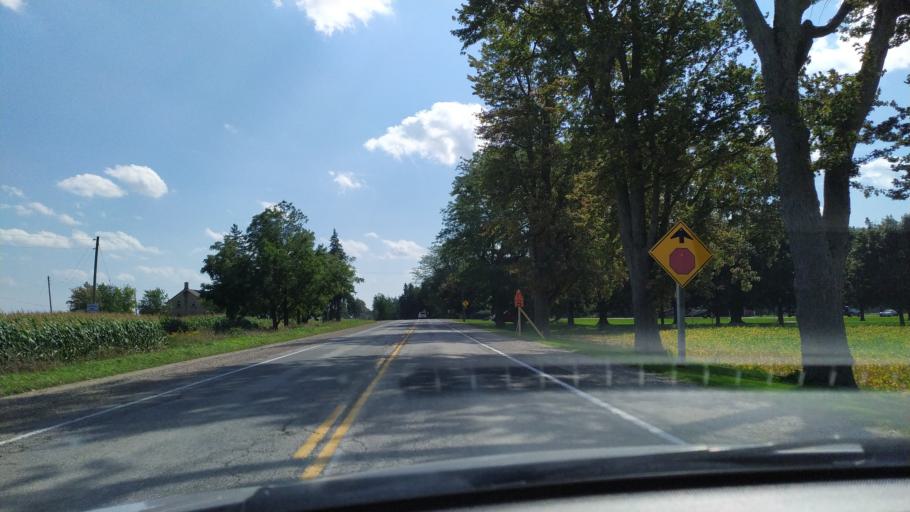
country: CA
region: Ontario
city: Stratford
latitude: 43.3193
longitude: -80.9863
